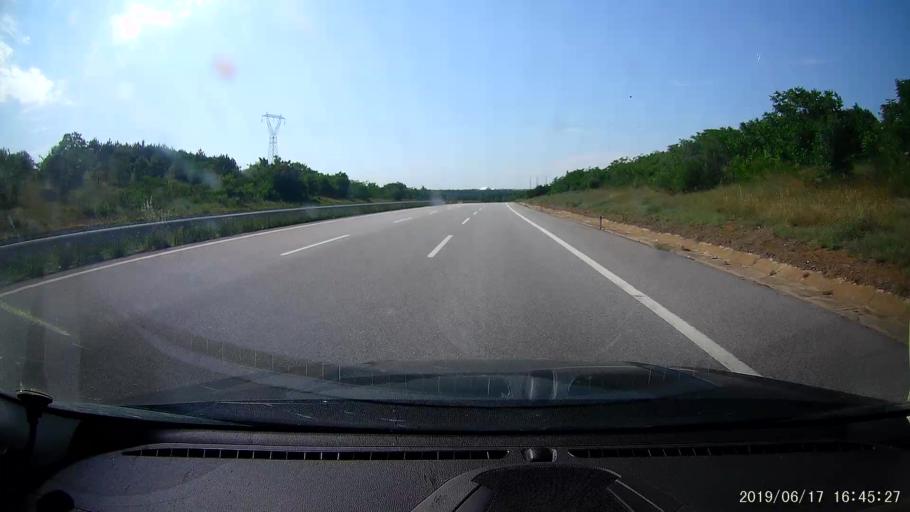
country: TR
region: Kirklareli
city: Babaeski
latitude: 41.4887
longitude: 27.2321
